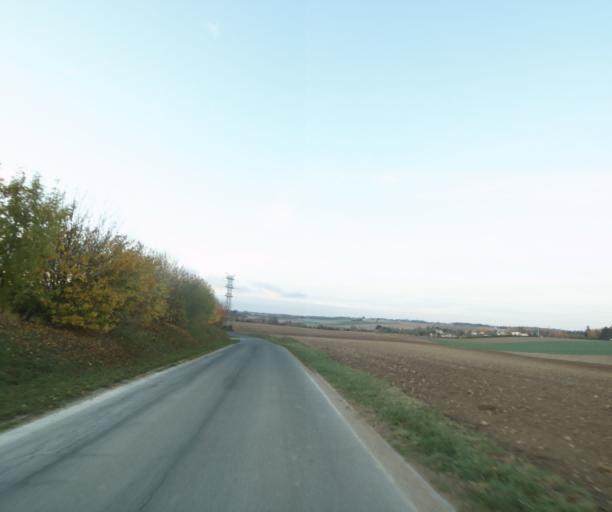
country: FR
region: Poitou-Charentes
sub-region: Departement de la Charente-Maritime
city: Saintes
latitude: 45.7623
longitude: -0.6504
